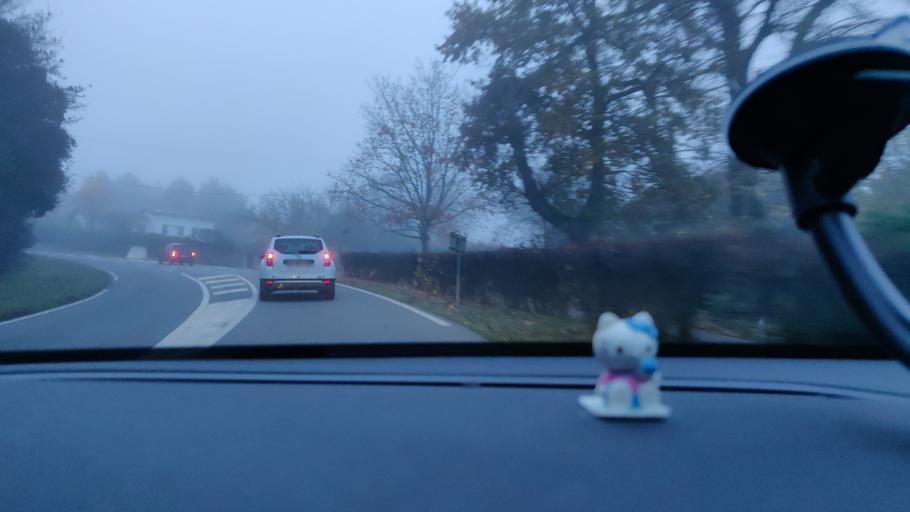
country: FR
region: Midi-Pyrenees
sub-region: Departement de la Haute-Garonne
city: Vieille-Toulouse
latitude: 43.5024
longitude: 1.4561
